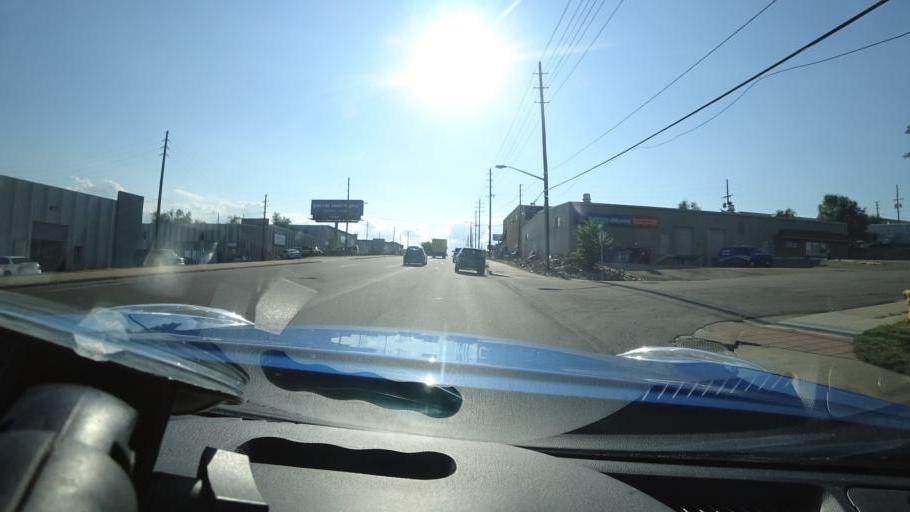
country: US
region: Colorado
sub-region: Arapahoe County
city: Englewood
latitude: 39.6786
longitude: -105.0051
